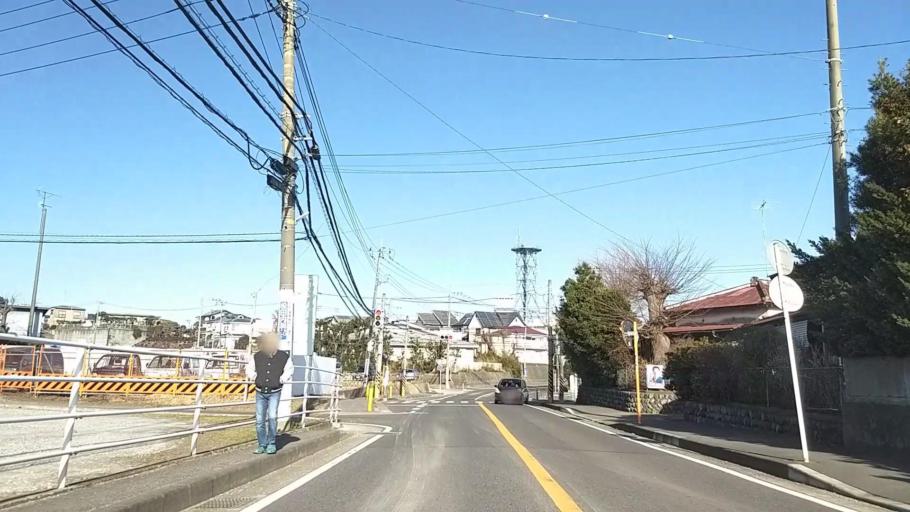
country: JP
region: Kanagawa
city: Atsugi
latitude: 35.4392
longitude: 139.3235
